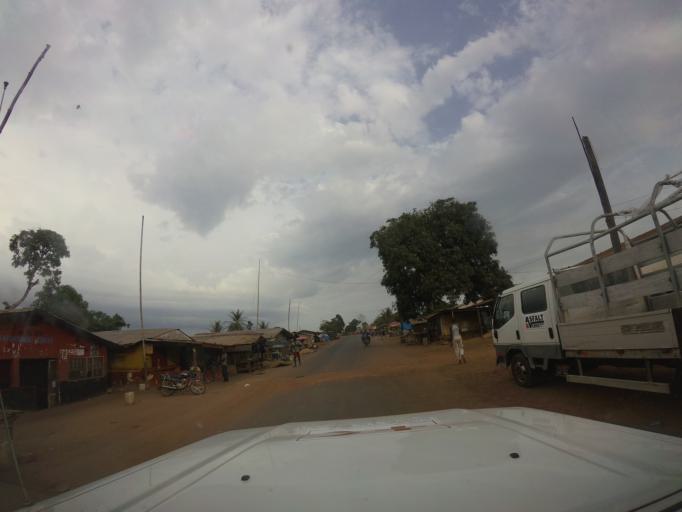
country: LR
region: Bomi
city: Tubmanburg
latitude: 6.7142
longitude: -10.9713
